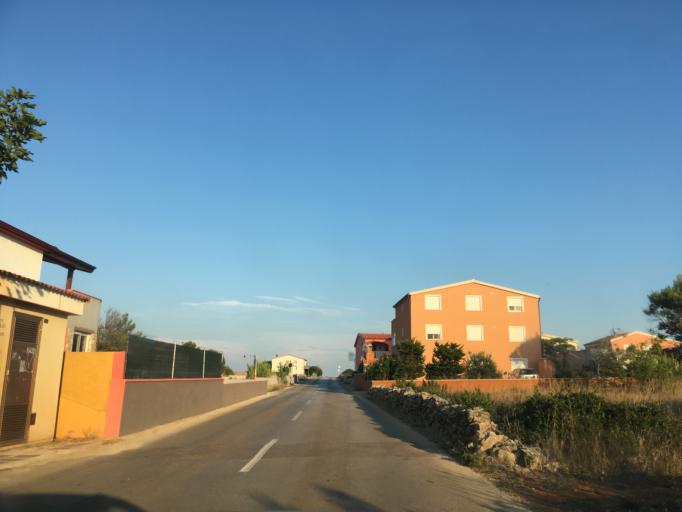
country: HR
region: Zadarska
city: Vir
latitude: 44.2995
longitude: 15.1123
